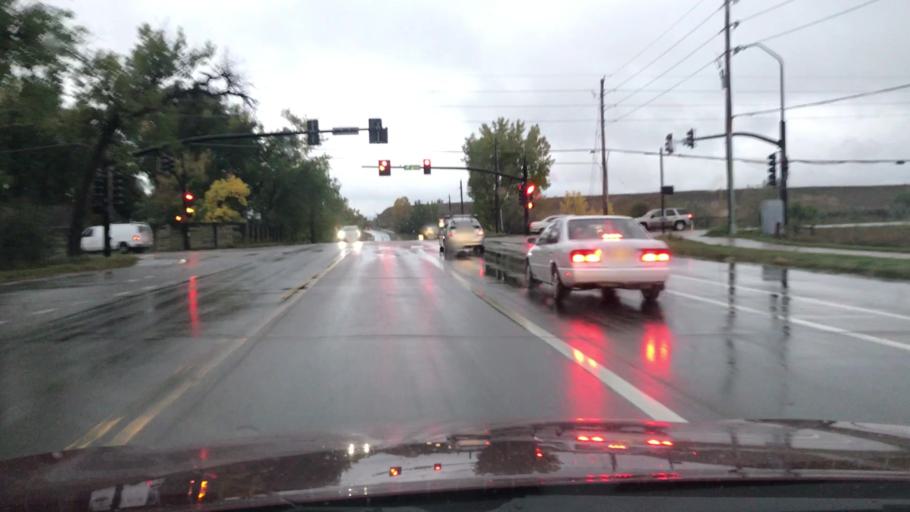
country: US
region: Colorado
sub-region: Boulder County
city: Gunbarrel
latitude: 40.0514
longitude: -105.2069
